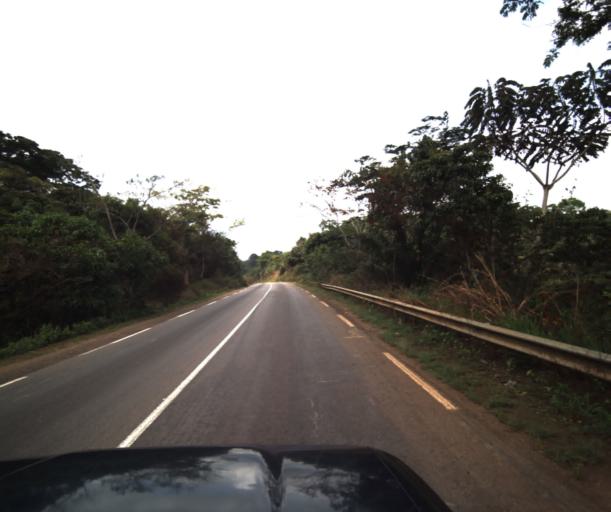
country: CM
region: Centre
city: Mbankomo
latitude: 3.7900
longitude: 11.2864
